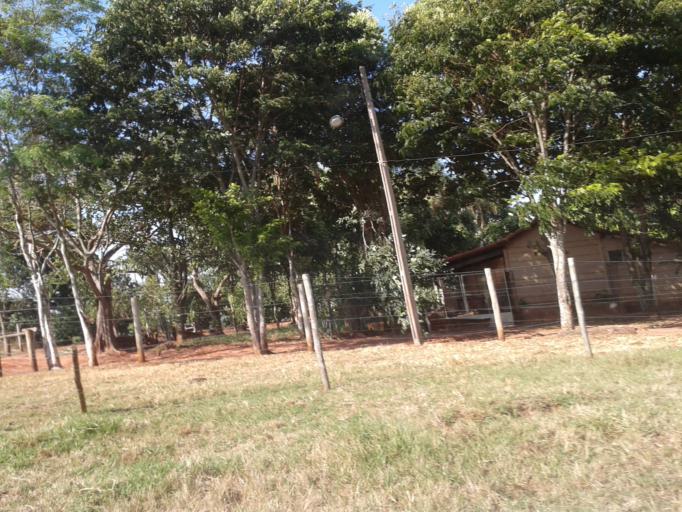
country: BR
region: Minas Gerais
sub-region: Campina Verde
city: Campina Verde
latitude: -19.4587
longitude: -49.6742
